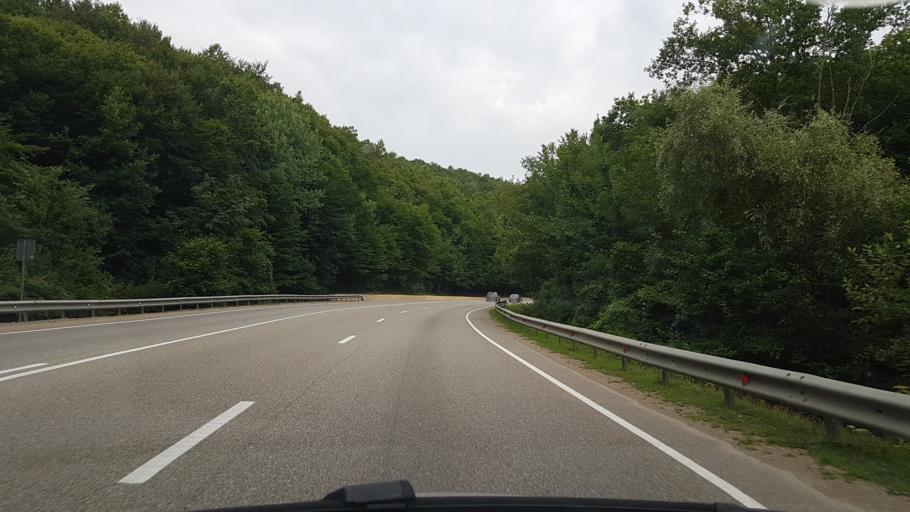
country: RU
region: Krasnodarskiy
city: Goryachiy Klyuch
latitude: 44.5485
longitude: 38.9825
